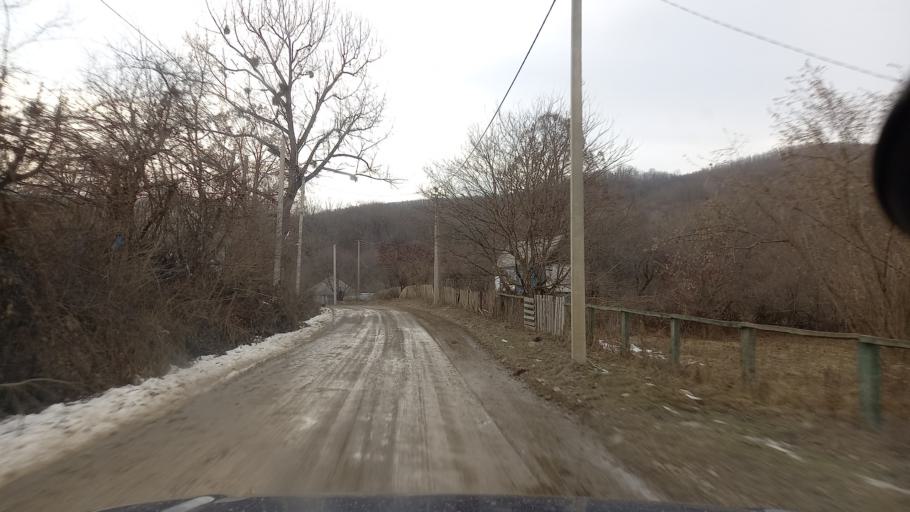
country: RU
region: Adygeya
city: Kamennomostskiy
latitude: 44.1422
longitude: 40.2779
